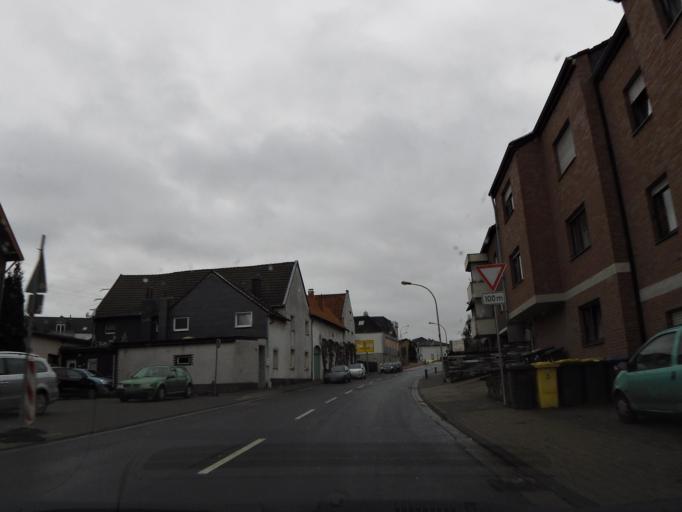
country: DE
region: North Rhine-Westphalia
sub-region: Regierungsbezirk Koln
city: Herzogenrath
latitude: 50.8750
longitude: 6.1058
